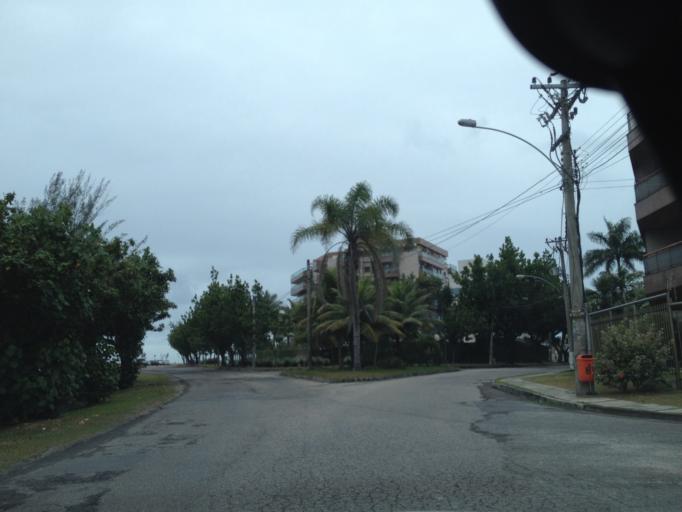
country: BR
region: Rio de Janeiro
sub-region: Nilopolis
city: Nilopolis
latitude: -23.0213
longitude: -43.4501
